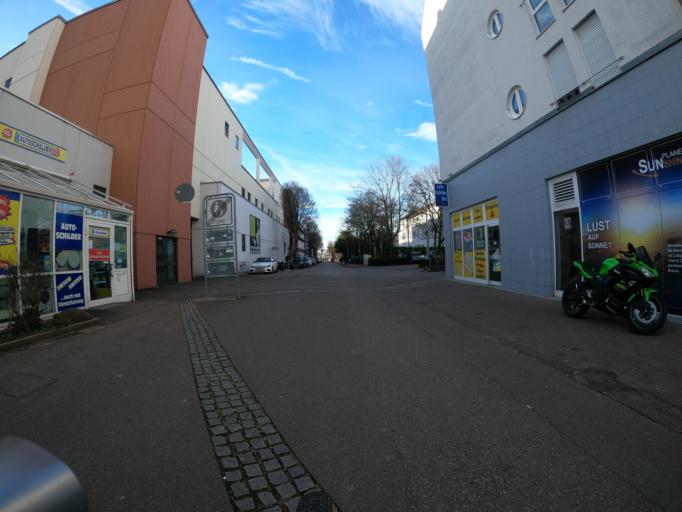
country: DE
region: Baden-Wuerttemberg
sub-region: Regierungsbezirk Stuttgart
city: Kirchheim unter Teck
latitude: 48.6498
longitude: 9.4462
